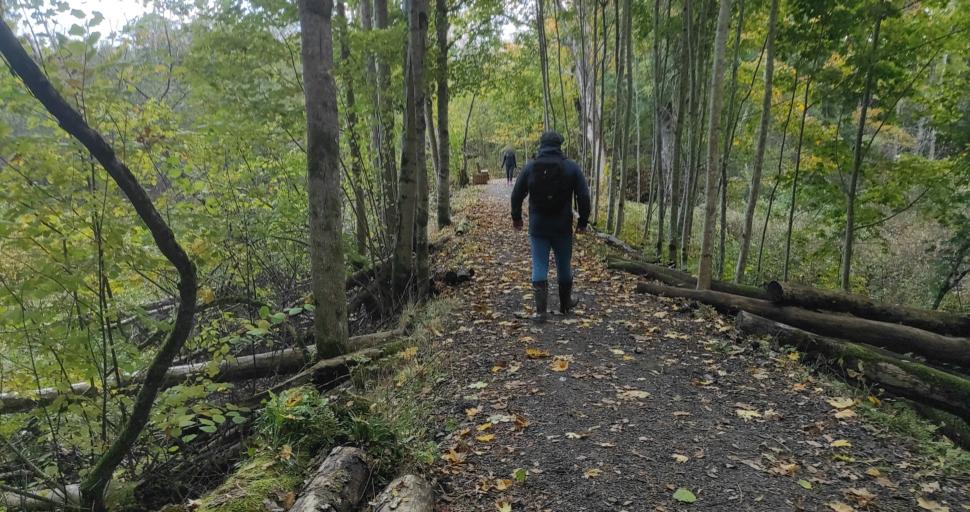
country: LV
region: Durbe
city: Liegi
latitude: 56.7258
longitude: 21.3743
